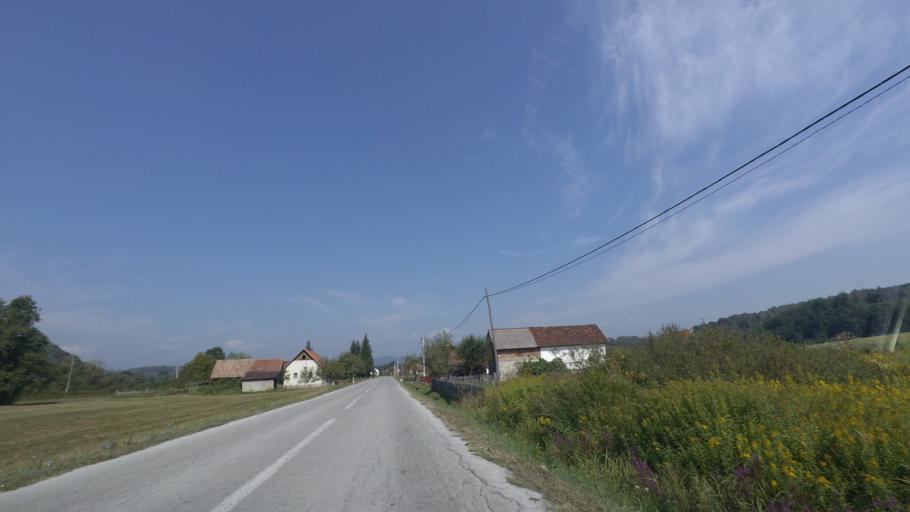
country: HR
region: Sisacko-Moslavacka
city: Dvor
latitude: 45.0935
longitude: 16.2973
